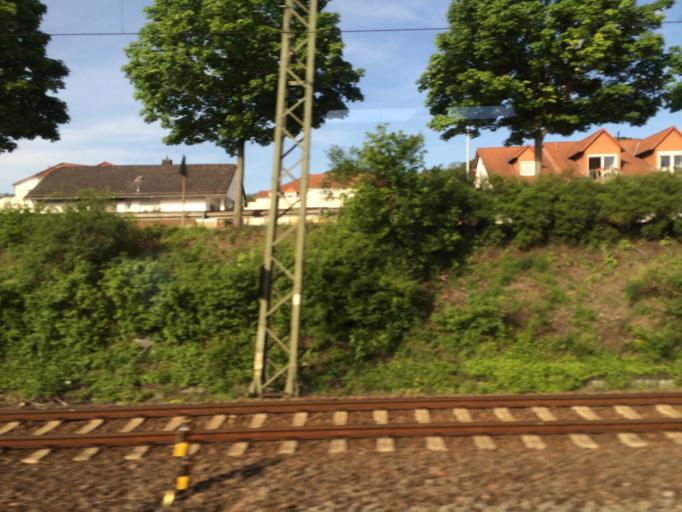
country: DE
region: Rheinland-Pfalz
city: Lahnstein
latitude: 50.2929
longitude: 7.6155
